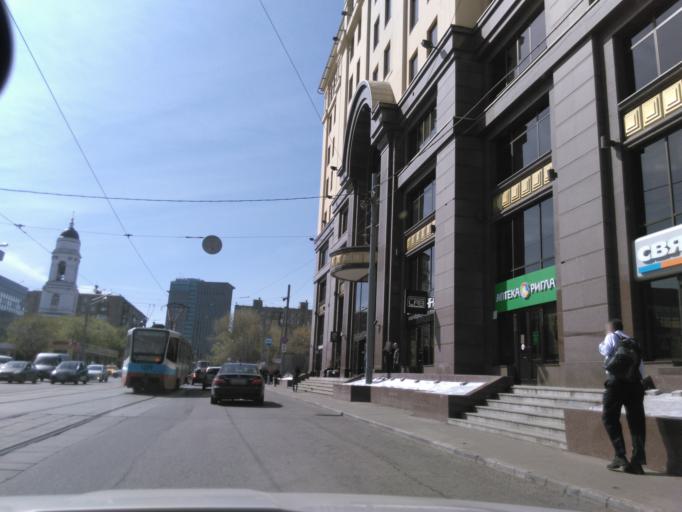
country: RU
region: Moscow
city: Zamoskvorech'ye
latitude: 55.7300
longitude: 37.6365
